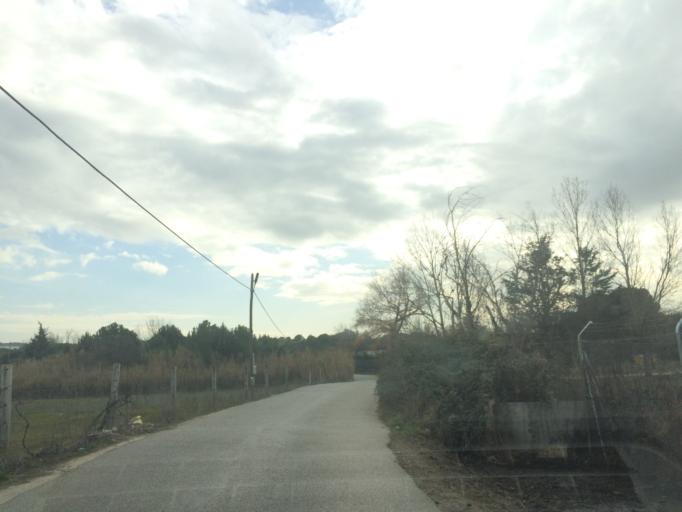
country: ES
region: Madrid
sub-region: Provincia de Madrid
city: Arroyomolinos
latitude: 40.3055
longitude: -3.9458
